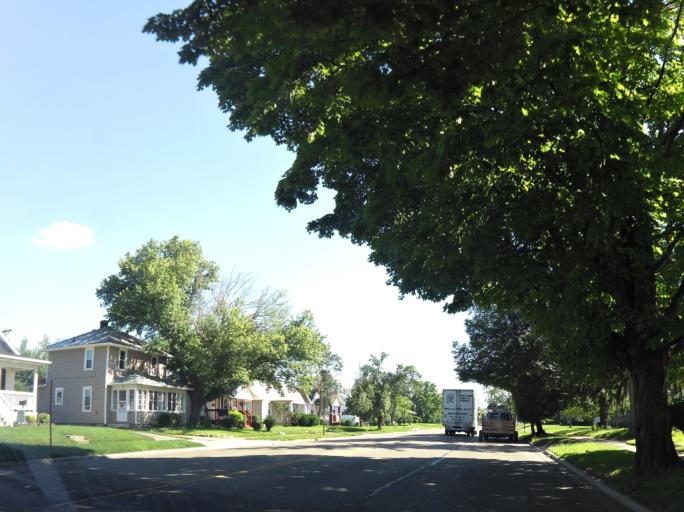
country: US
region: Ohio
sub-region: Greene County
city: Fairborn
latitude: 39.8287
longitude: -84.0200
